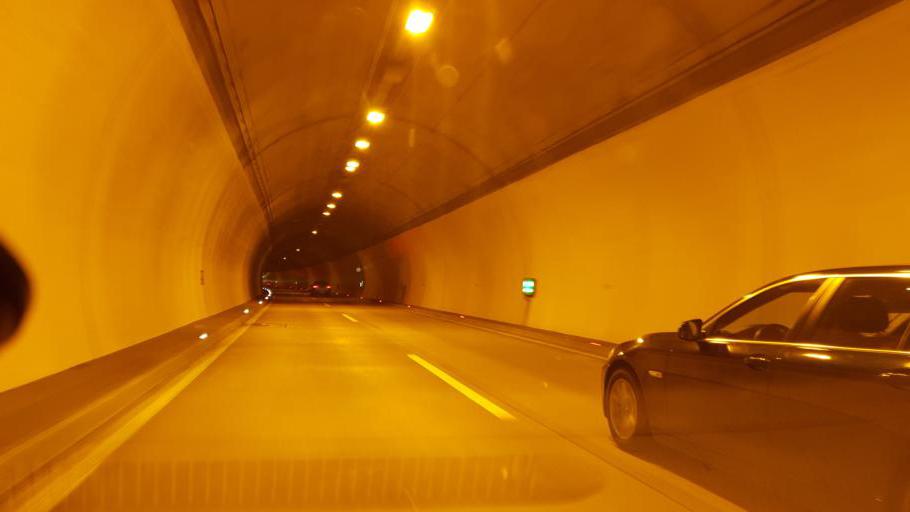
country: AT
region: Carinthia
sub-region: Politischer Bezirk Villach Land
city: Fresach
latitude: 46.6653
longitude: 13.7183
